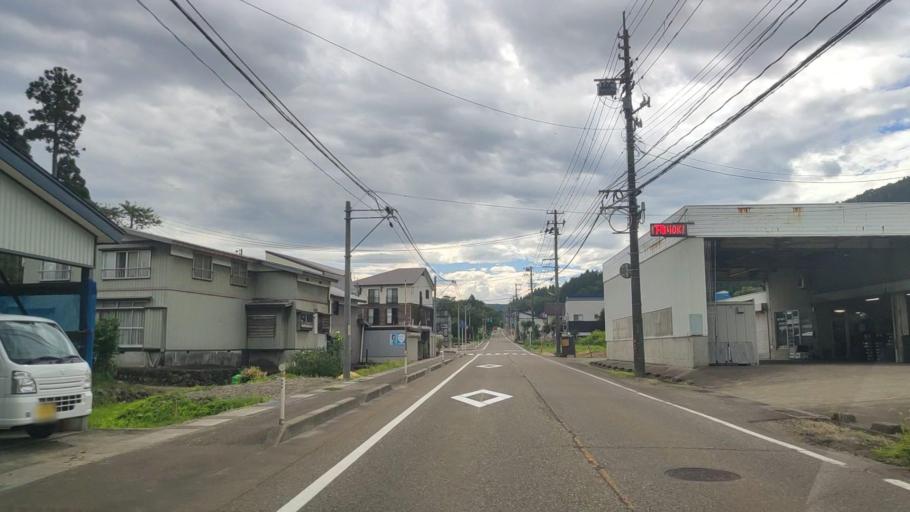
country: JP
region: Niigata
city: Arai
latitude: 37.0024
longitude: 138.2639
